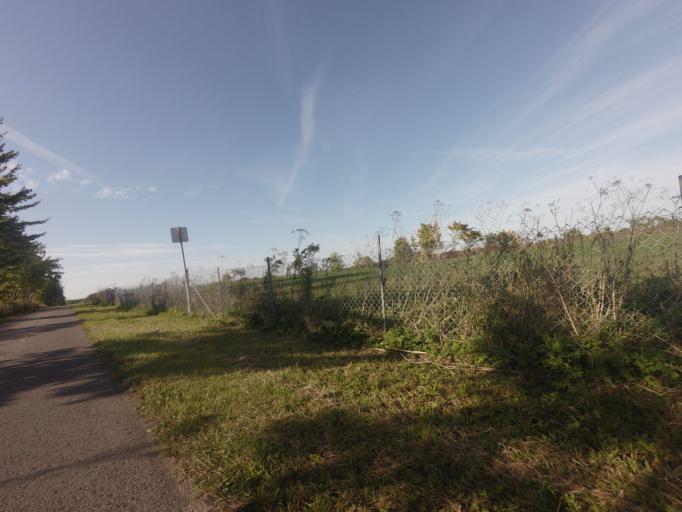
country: CA
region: Quebec
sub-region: Laurentides
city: Blainville
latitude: 45.7179
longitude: -73.9264
